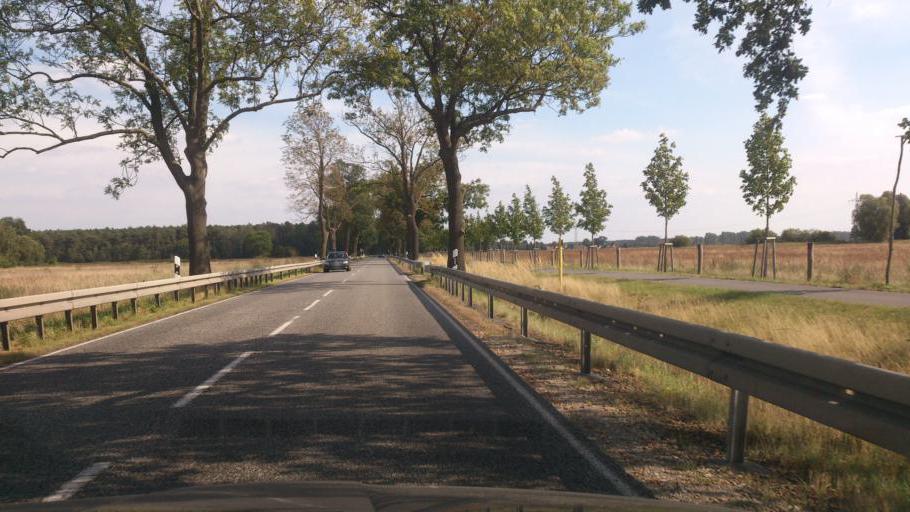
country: DE
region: Brandenburg
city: Stahnsdorf
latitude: 52.3260
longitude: 13.1796
